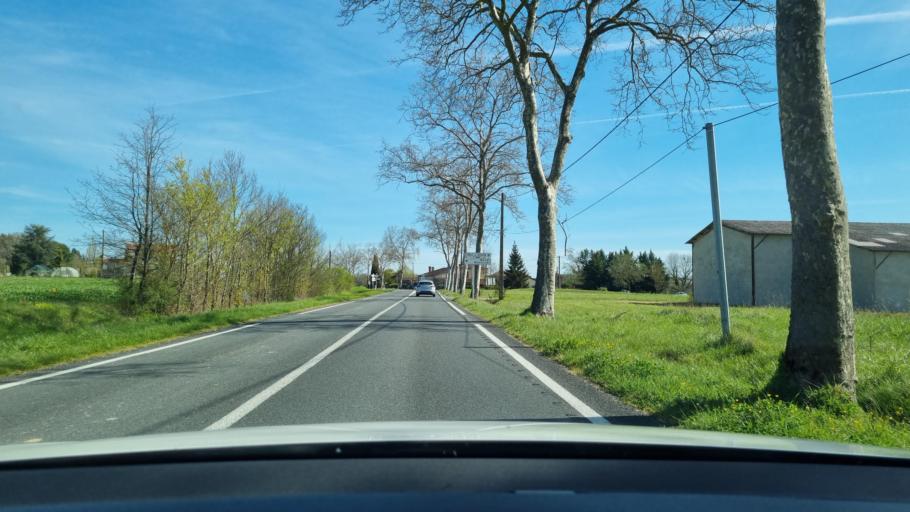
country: FR
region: Midi-Pyrenees
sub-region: Departement du Gers
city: Lombez
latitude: 43.3973
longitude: 0.7927
